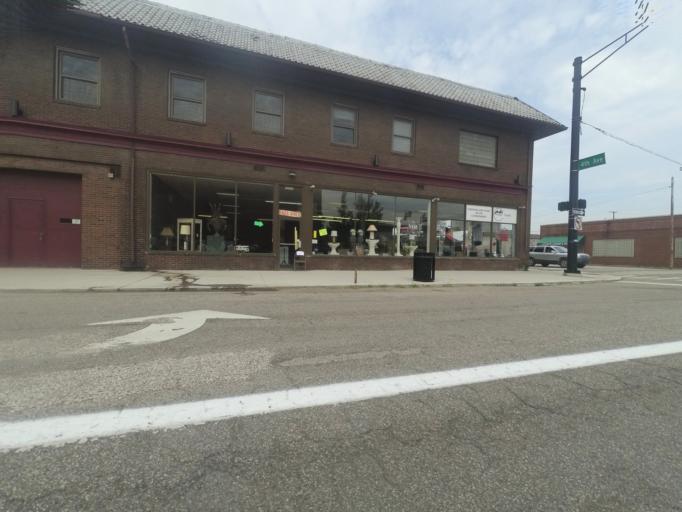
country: US
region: West Virginia
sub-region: Cabell County
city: Huntington
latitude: 38.4196
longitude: -82.4489
